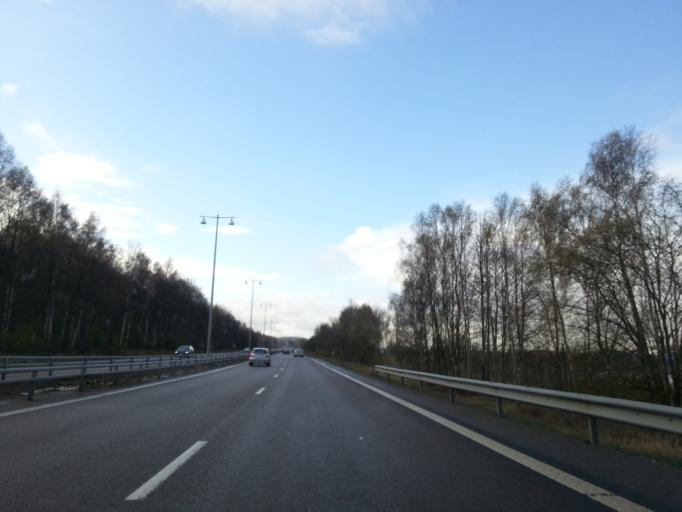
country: SE
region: Vaestra Goetaland
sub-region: Goteborg
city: Hammarkullen
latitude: 57.7796
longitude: 12.0076
